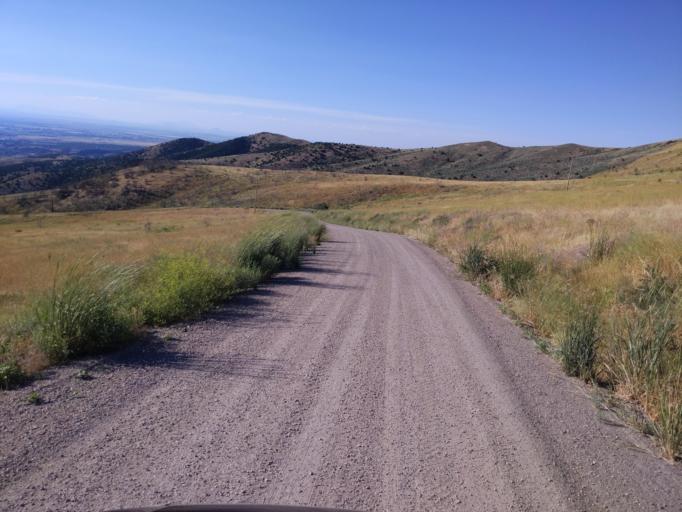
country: US
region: Idaho
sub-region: Bannock County
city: Pocatello
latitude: 42.8490
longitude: -112.3705
